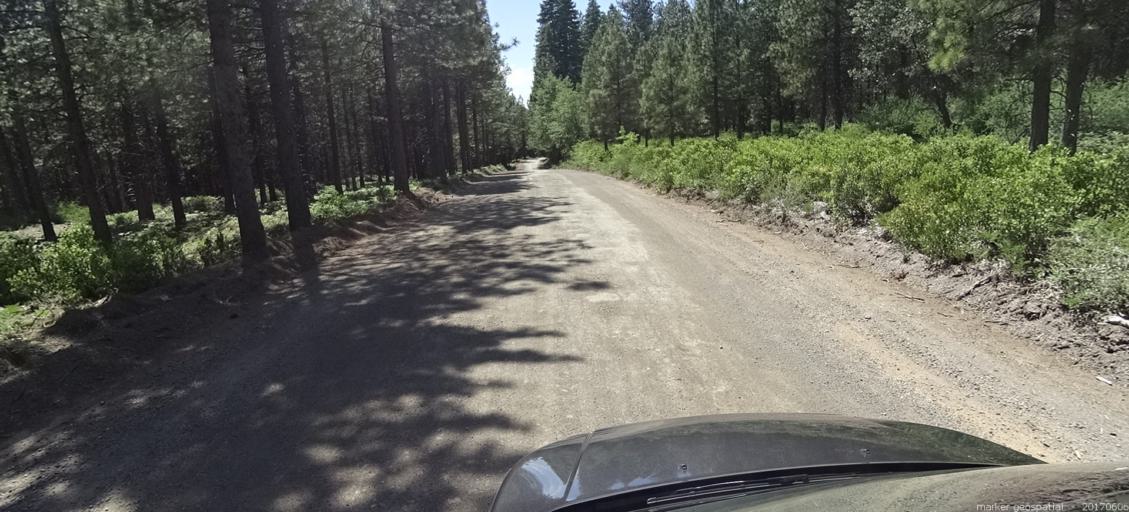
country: US
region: California
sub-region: Siskiyou County
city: Mount Shasta
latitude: 41.2745
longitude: -122.2927
